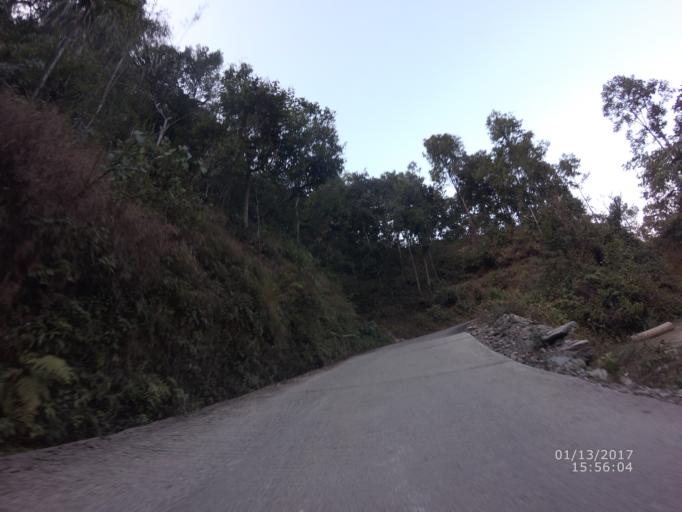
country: NP
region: Western Region
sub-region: Gandaki Zone
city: Pokhara
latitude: 28.1577
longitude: 84.0023
